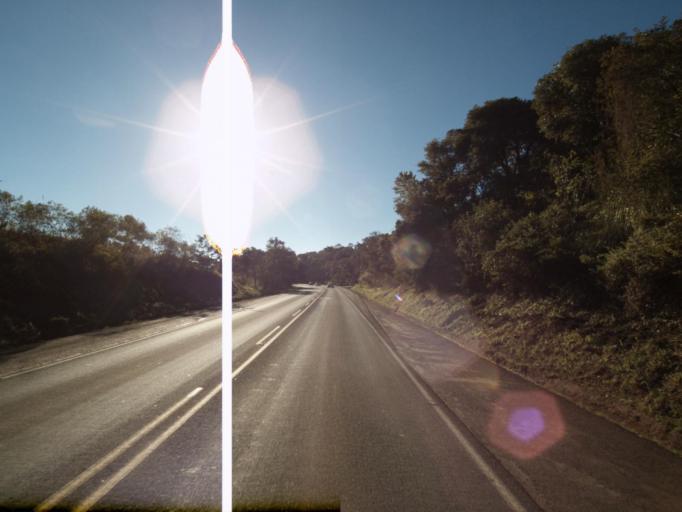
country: BR
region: Santa Catarina
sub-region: Chapeco
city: Chapeco
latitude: -26.9929
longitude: -52.7245
